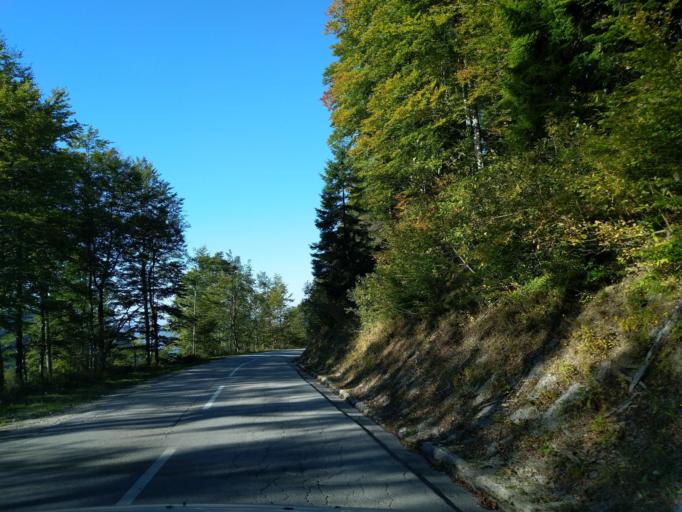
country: RS
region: Central Serbia
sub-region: Moravicki Okrug
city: Ivanjica
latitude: 43.4348
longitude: 20.2678
